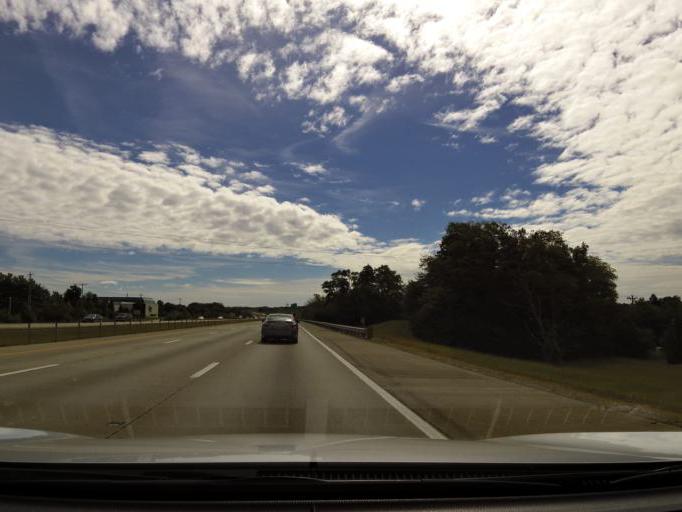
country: US
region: Kentucky
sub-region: Kenton County
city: Villa Hills
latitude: 39.0483
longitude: -84.6190
